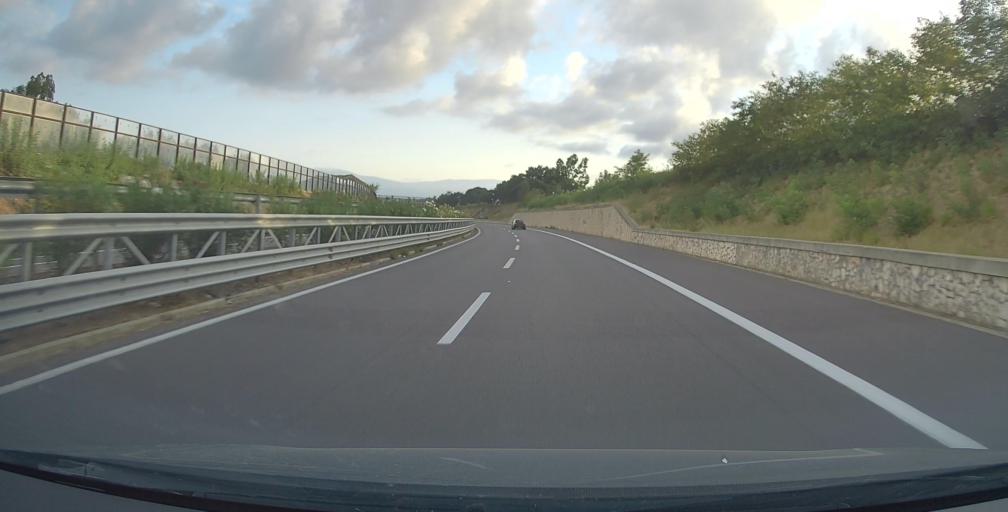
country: IT
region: Calabria
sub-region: Provincia di Catanzaro
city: Acconia
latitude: 38.8678
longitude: 16.2807
